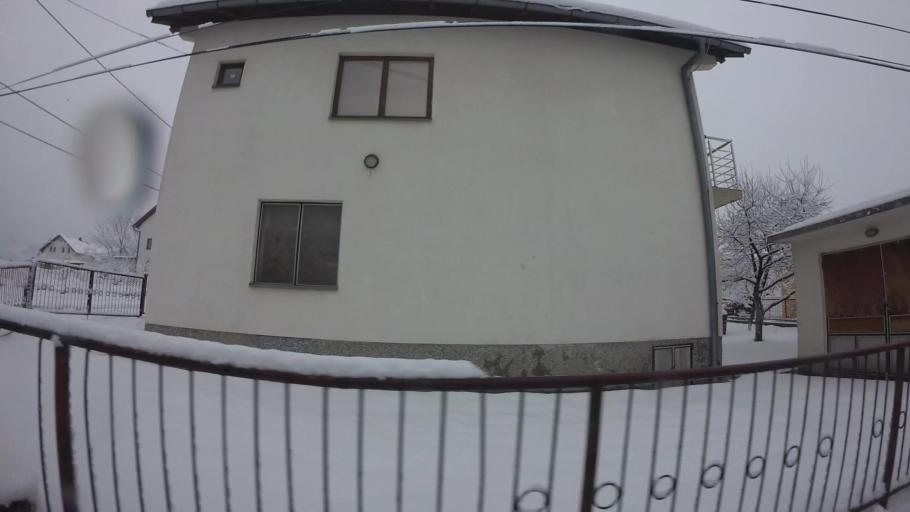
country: BA
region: Federation of Bosnia and Herzegovina
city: Vogosca
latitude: 43.8702
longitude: 18.3175
